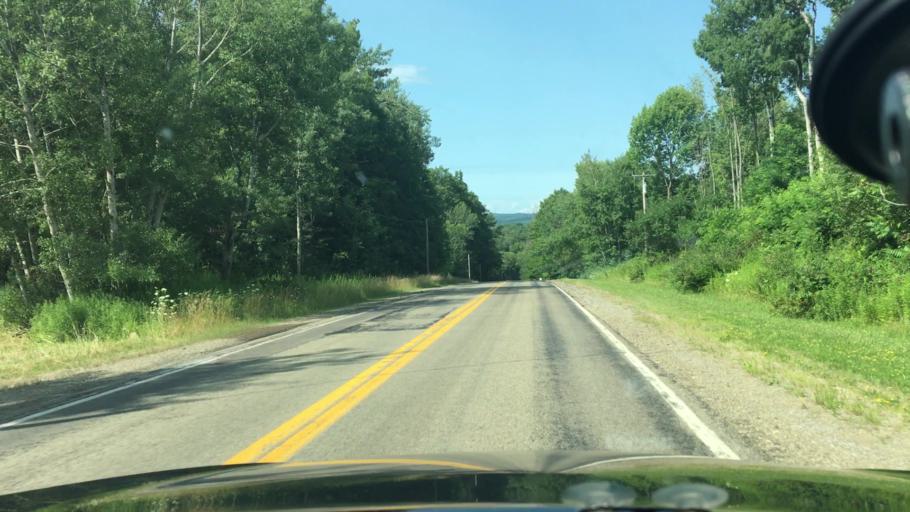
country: US
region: New York
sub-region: Chautauqua County
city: Lakewood
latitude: 42.2479
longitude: -79.3569
